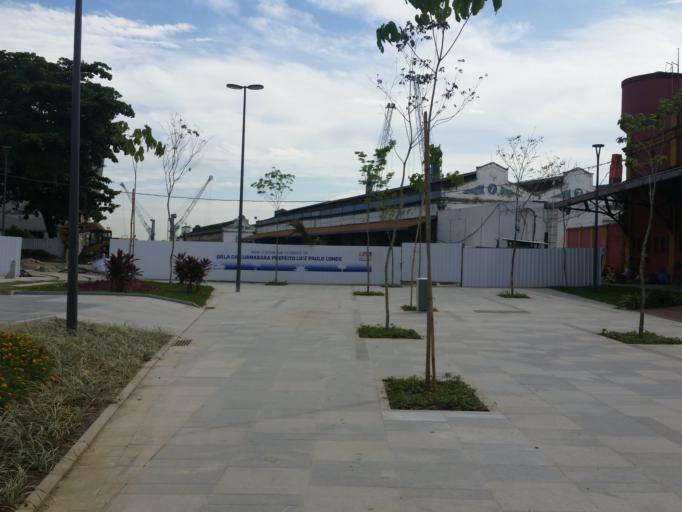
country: BR
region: Rio de Janeiro
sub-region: Rio De Janeiro
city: Rio de Janeiro
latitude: -22.8931
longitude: -43.1904
